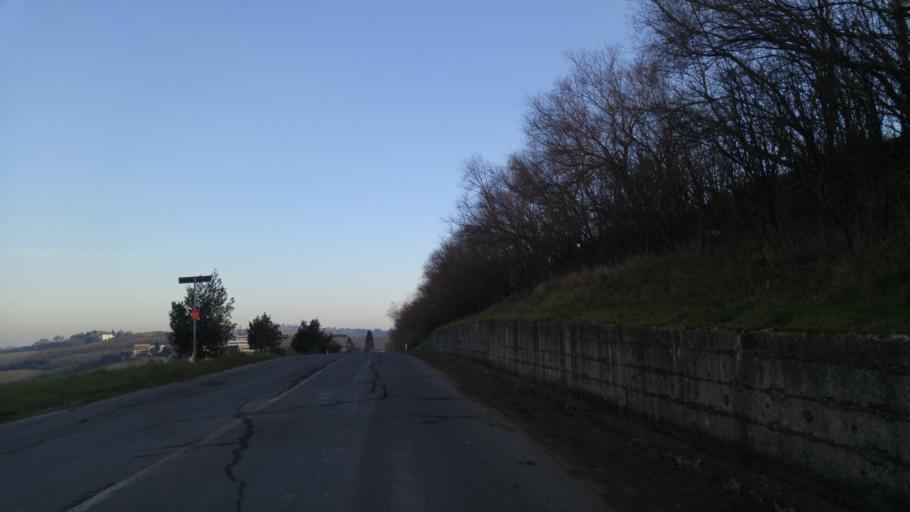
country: IT
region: The Marches
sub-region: Provincia di Pesaro e Urbino
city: San Giorgio di Pesaro
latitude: 43.7104
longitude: 12.9884
